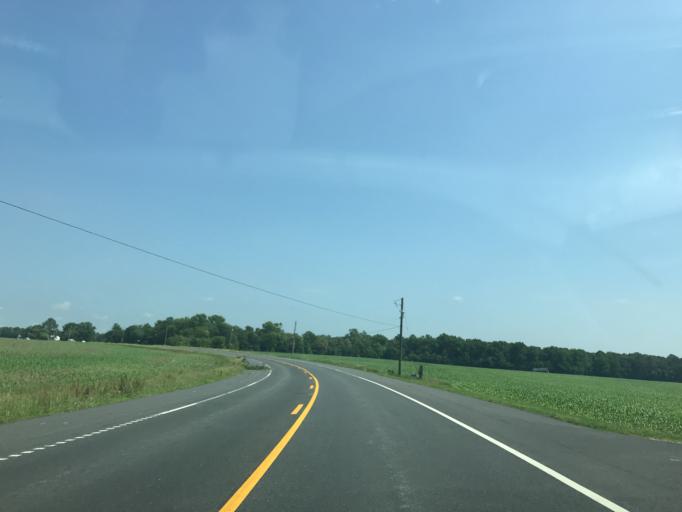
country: US
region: Maryland
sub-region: Wicomico County
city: Hebron
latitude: 38.5258
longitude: -75.7113
